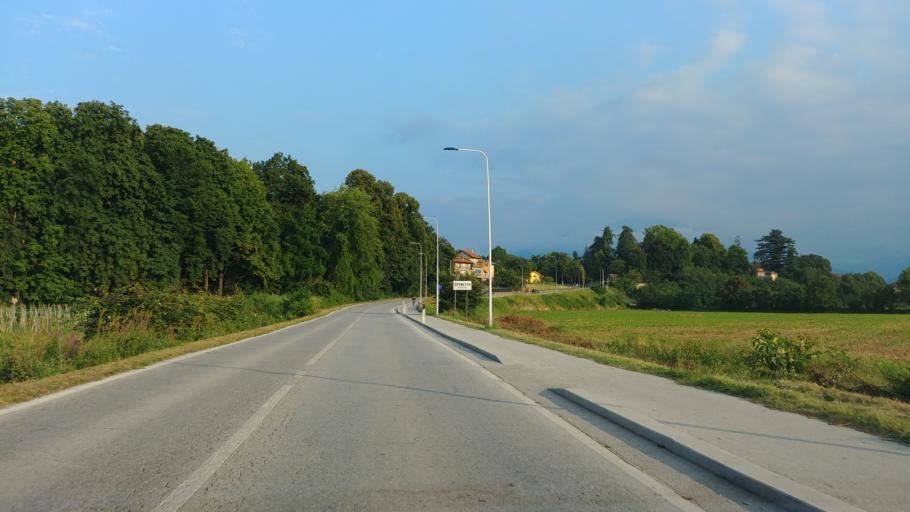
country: IT
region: Piedmont
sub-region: Provincia di Cuneo
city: Cuneo
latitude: 44.3830
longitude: 7.5676
